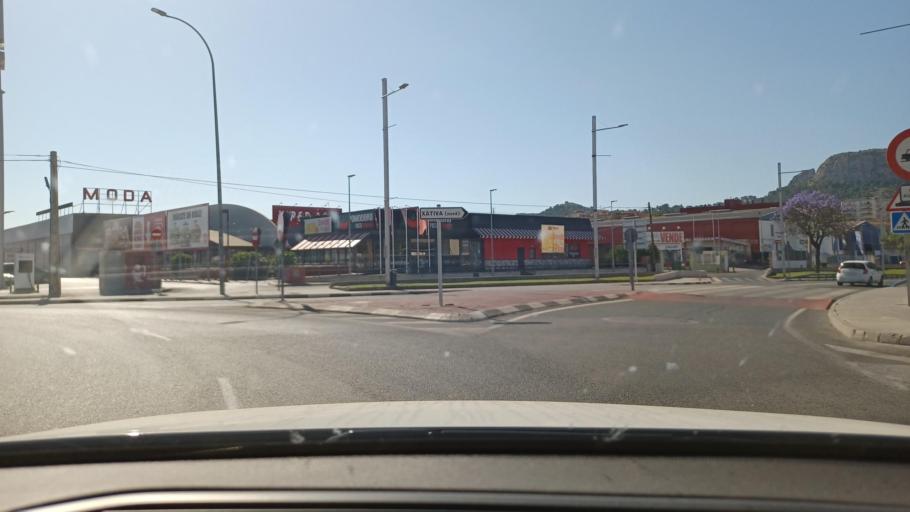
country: ES
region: Valencia
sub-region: Provincia de Valencia
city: Xativa
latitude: 38.9960
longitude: -0.5212
